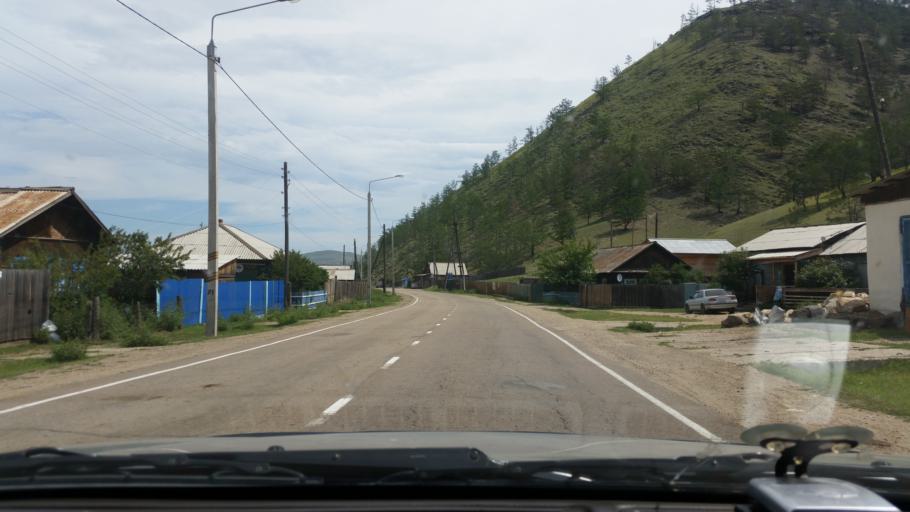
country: RU
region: Irkutsk
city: Yelantsy
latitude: 52.7977
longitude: 106.4136
